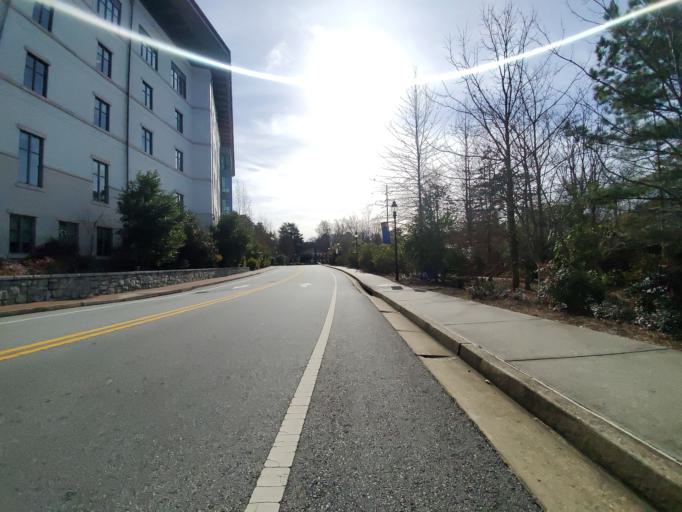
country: US
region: Georgia
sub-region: DeKalb County
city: Druid Hills
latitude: 33.7915
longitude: -84.3275
